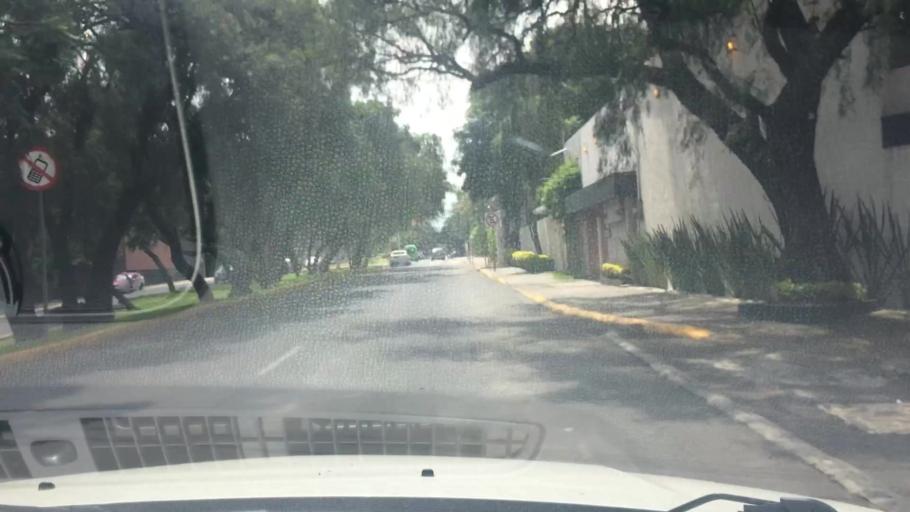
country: MX
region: Mexico City
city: Magdalena Contreras
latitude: 19.3176
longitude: -99.2022
